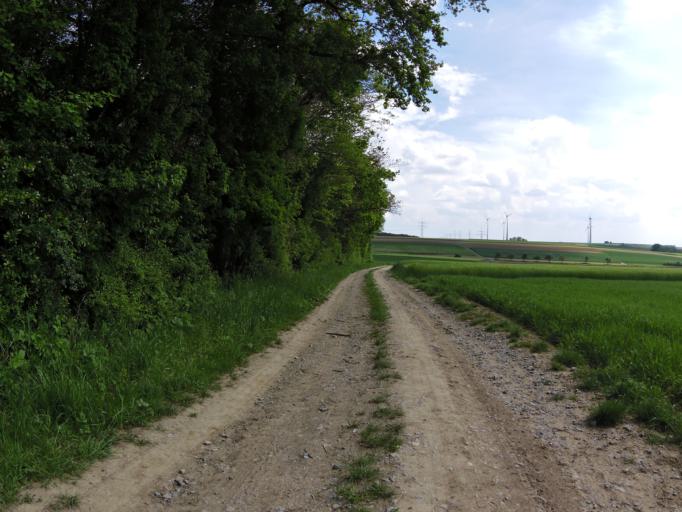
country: DE
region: Bavaria
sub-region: Regierungsbezirk Unterfranken
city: Theilheim
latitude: 49.7435
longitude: 10.0394
